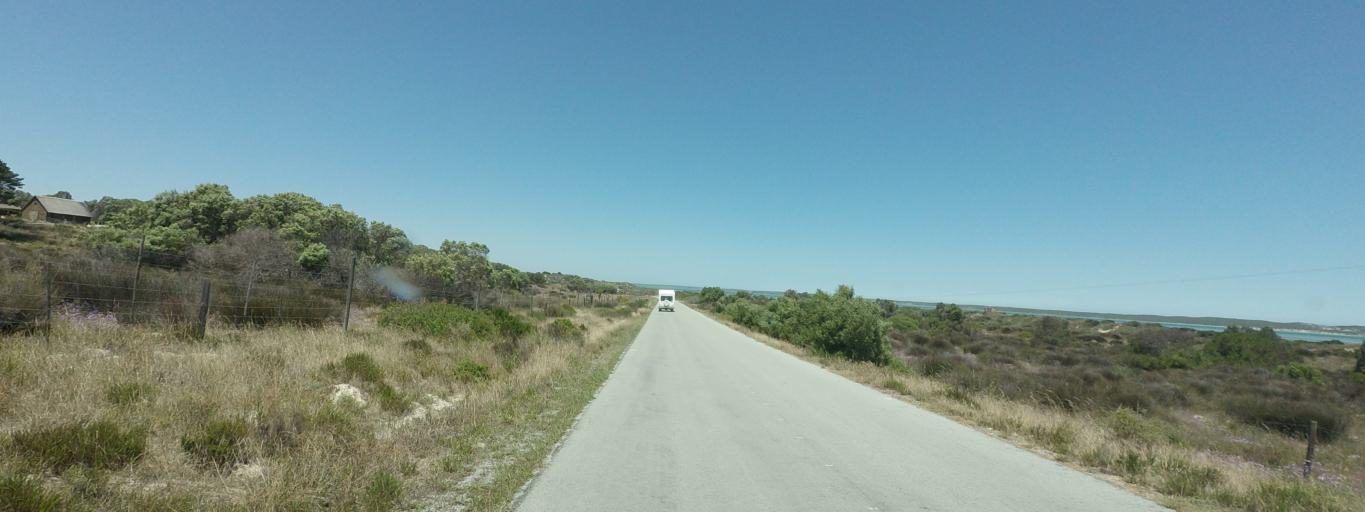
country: ZA
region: Western Cape
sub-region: West Coast District Municipality
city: Saldanha
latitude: -33.1145
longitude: 18.0529
